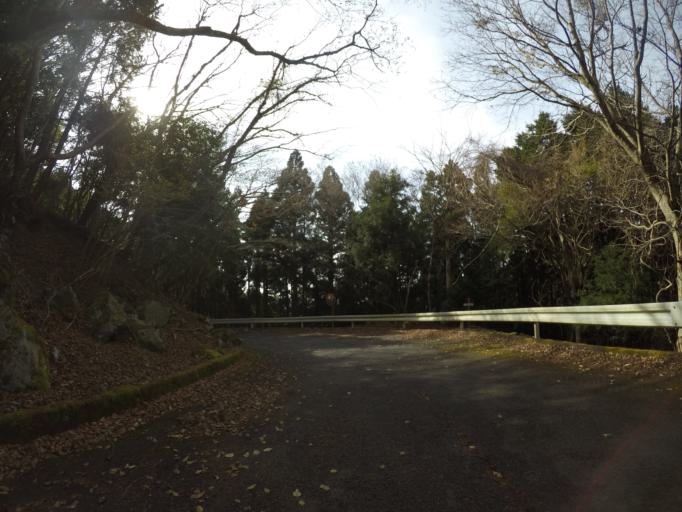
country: JP
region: Shizuoka
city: Heda
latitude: 34.8397
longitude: 138.8489
